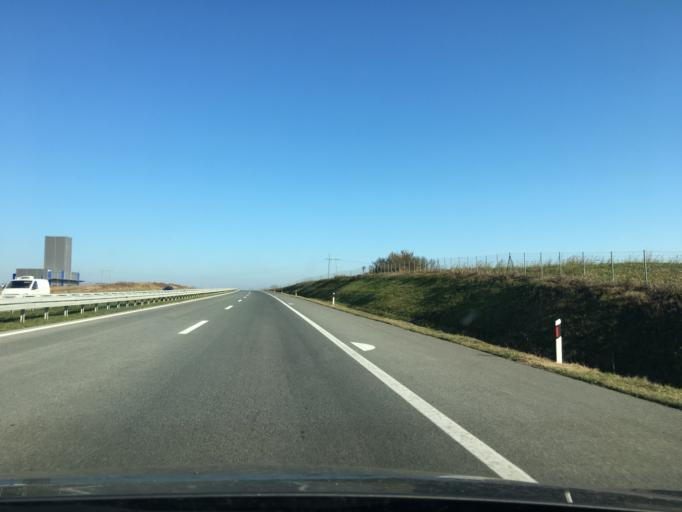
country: RS
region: Autonomna Pokrajina Vojvodina
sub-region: Severnobacki Okrug
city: Mali Igos
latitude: 45.6511
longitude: 19.7209
